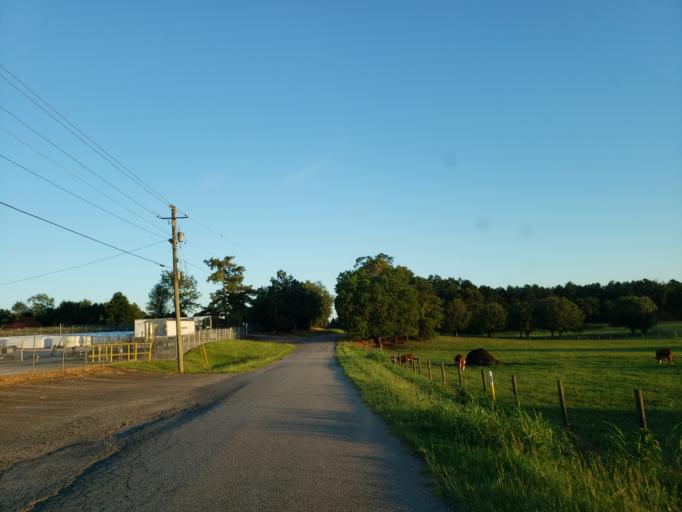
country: US
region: Georgia
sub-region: Bartow County
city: Euharlee
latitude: 34.1143
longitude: -84.8828
